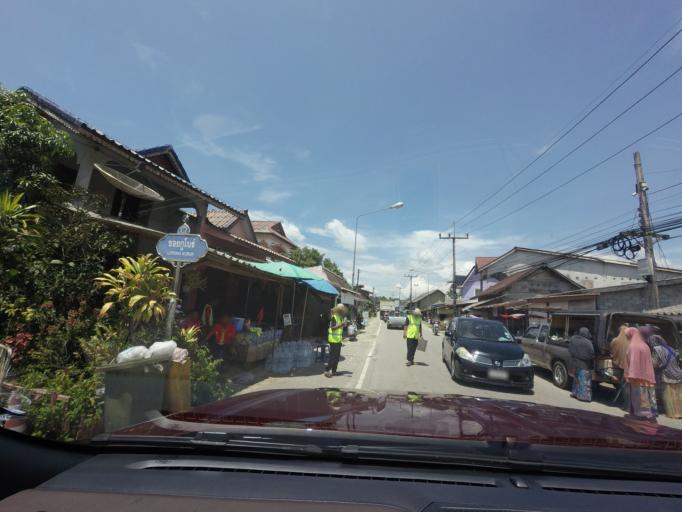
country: TH
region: Narathiwat
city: Chanae
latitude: 6.1294
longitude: 101.6980
